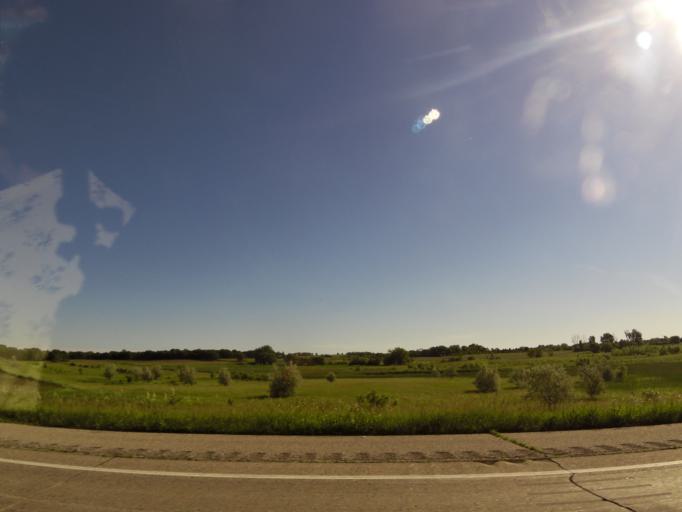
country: US
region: Minnesota
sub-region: Grant County
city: Elbow Lake
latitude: 46.0841
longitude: -95.8846
